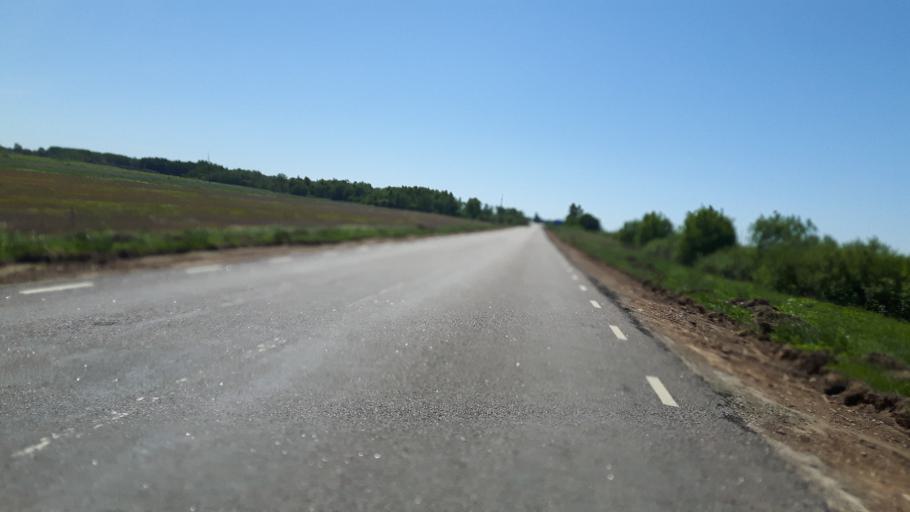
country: EE
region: Ida-Virumaa
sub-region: Narva-Joesuu linn
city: Narva-Joesuu
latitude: 59.3849
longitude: 27.9206
